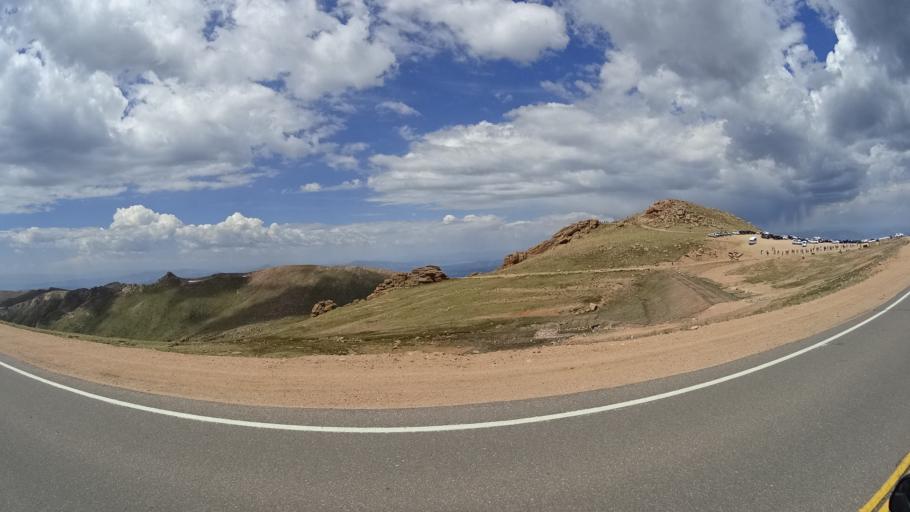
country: US
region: Colorado
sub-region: El Paso County
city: Cascade-Chipita Park
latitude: 38.8620
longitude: -105.0671
